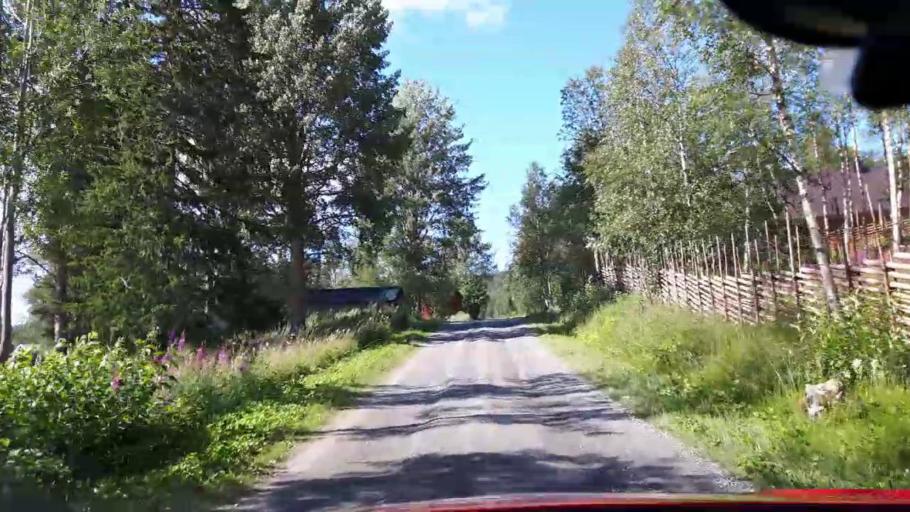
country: SE
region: Jaemtland
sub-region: Are Kommun
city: Are
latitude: 63.2106
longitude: 13.0550
